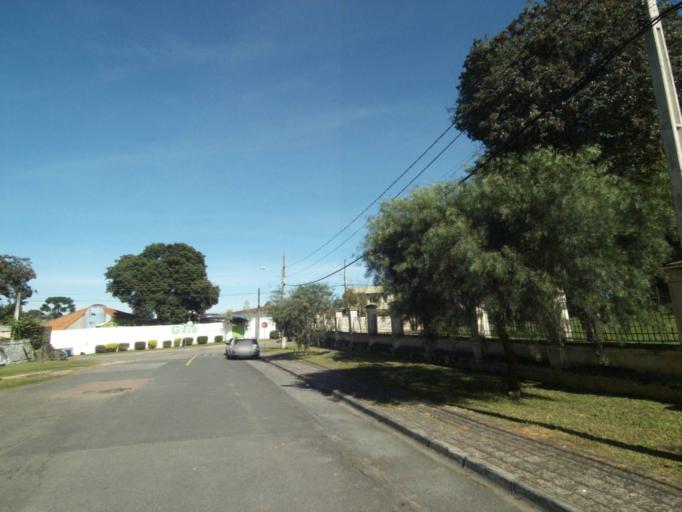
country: BR
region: Parana
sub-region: Curitiba
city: Curitiba
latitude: -25.4367
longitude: -49.2960
